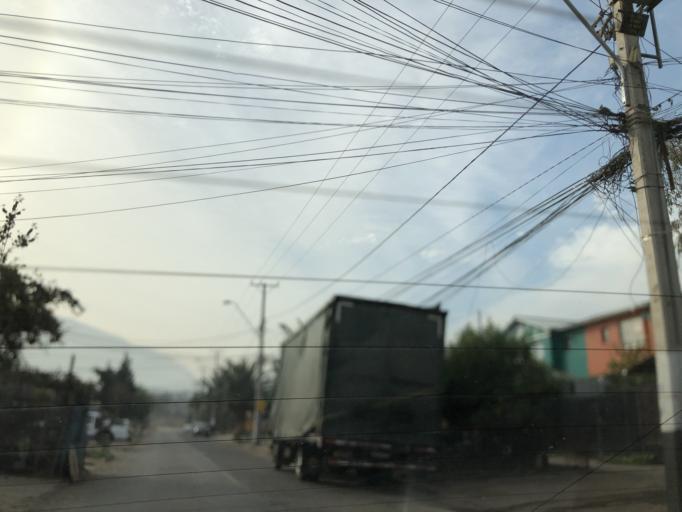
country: CL
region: Santiago Metropolitan
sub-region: Provincia de Cordillera
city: Puente Alto
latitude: -33.5839
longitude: -70.5521
